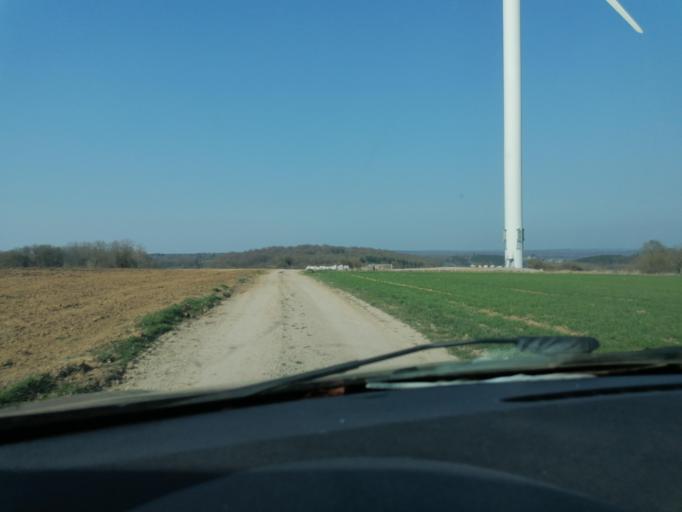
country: BE
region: Wallonia
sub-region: Province du Hainaut
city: Chimay
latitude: 50.0460
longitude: 4.3854
